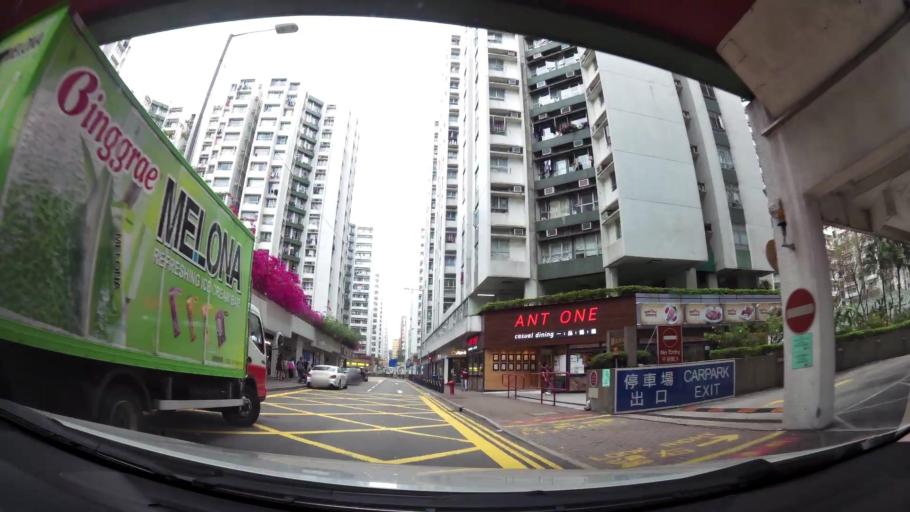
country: HK
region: Kowloon City
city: Kowloon
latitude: 22.3039
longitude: 114.1888
